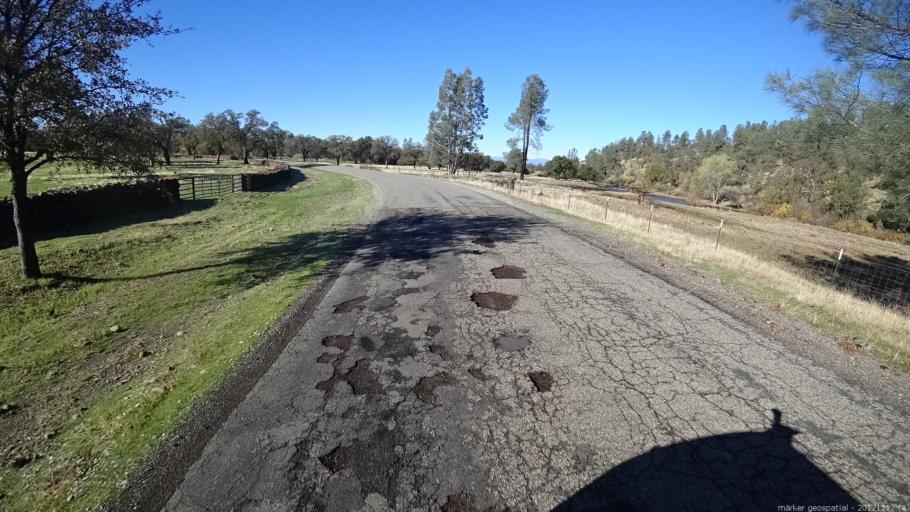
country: US
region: California
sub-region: Shasta County
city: Cottonwood
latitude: 40.4420
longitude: -122.1597
